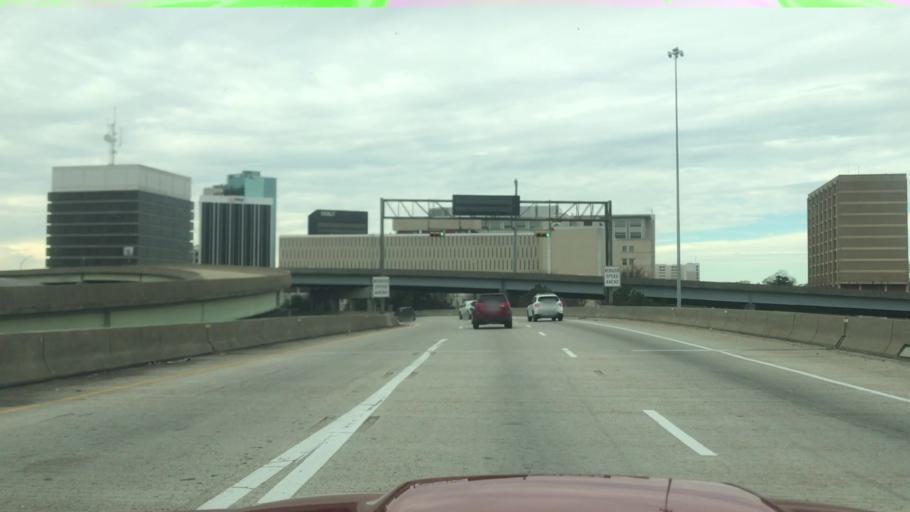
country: US
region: Virginia
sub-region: City of Norfolk
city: Norfolk
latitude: 36.8451
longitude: -76.2819
